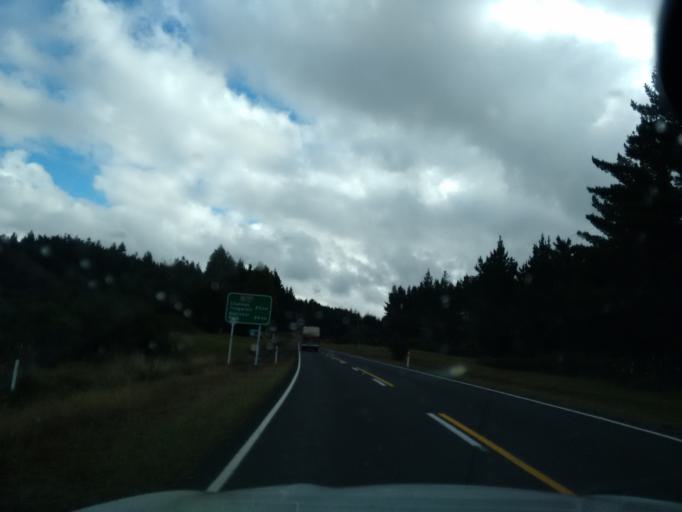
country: NZ
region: Waikato
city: Turangi
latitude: -39.0449
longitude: 175.6053
